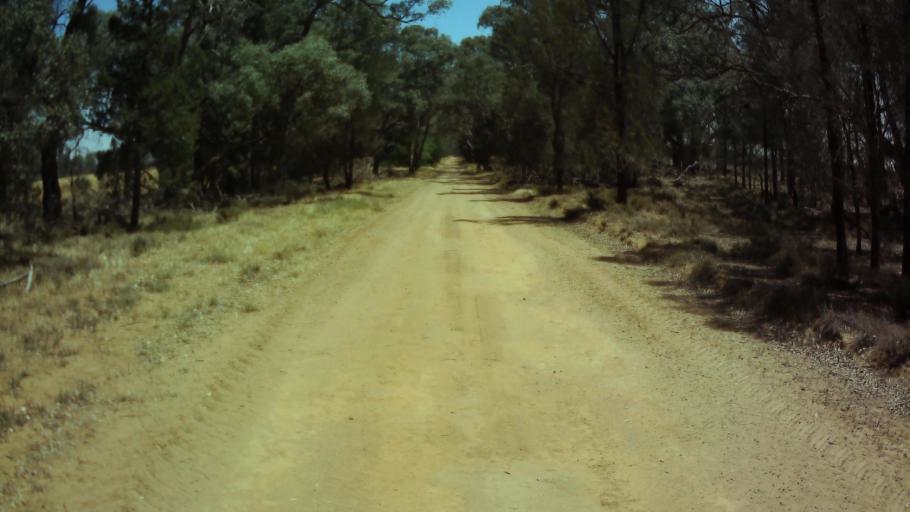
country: AU
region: New South Wales
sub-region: Weddin
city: Grenfell
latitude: -34.0404
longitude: 147.8482
